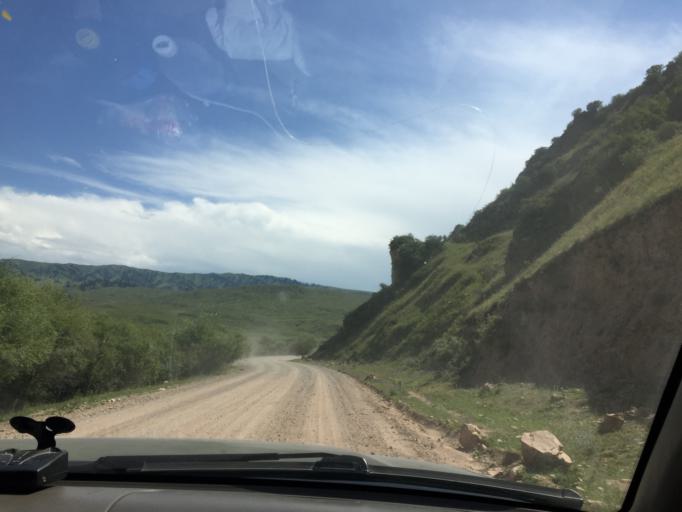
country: KZ
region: Almaty Oblysy
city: Kegen
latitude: 42.7444
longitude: 78.9518
